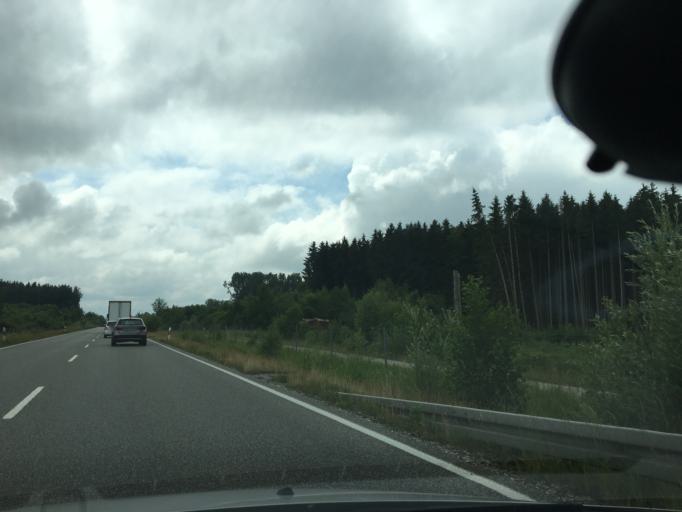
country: DE
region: Bavaria
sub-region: Upper Bavaria
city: Poing
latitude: 48.1877
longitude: 11.8397
